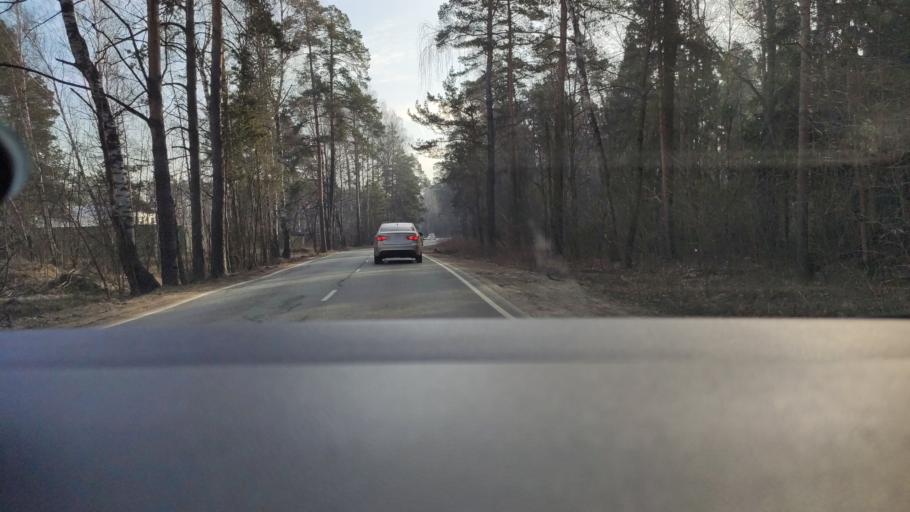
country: RU
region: Moskovskaya
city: Zarya
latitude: 55.8068
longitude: 38.0987
